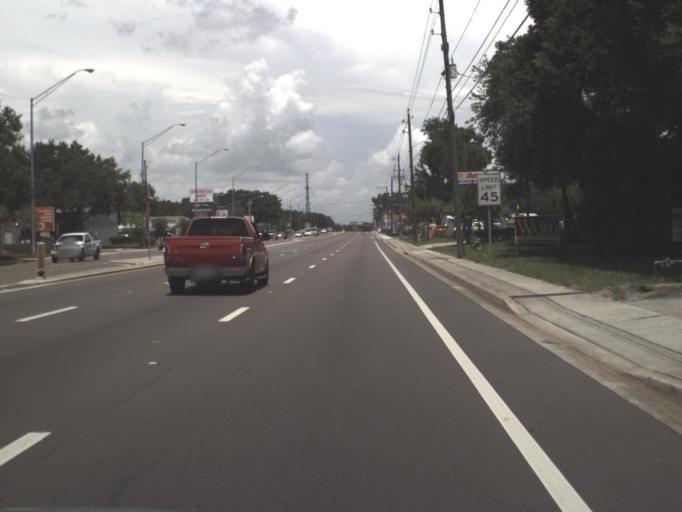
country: US
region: Florida
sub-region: Hillsborough County
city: Riverview
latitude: 27.8731
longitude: -82.3266
